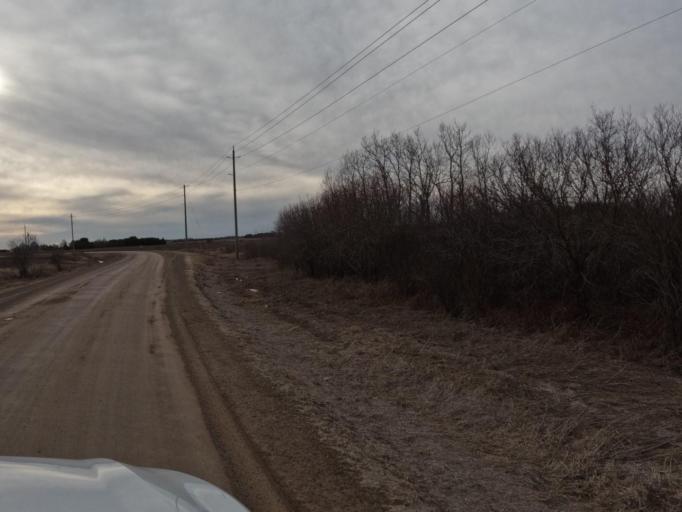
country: CA
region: Ontario
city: Orangeville
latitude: 43.9196
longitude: -80.2277
